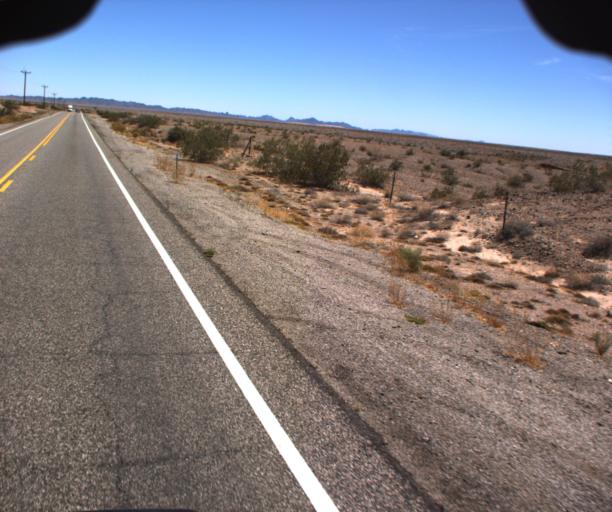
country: US
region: Arizona
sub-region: La Paz County
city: Parker
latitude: 34.0073
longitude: -114.2409
